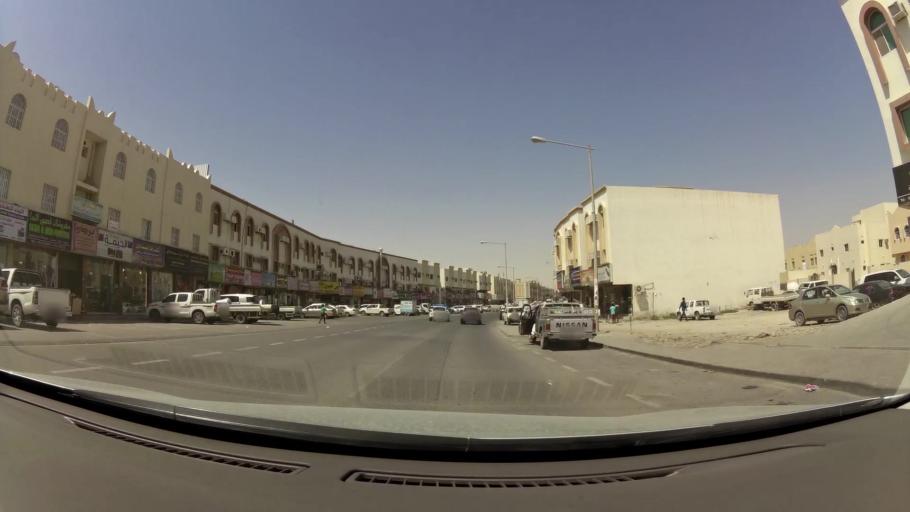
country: QA
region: Baladiyat ar Rayyan
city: Ar Rayyan
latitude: 25.2724
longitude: 51.4080
